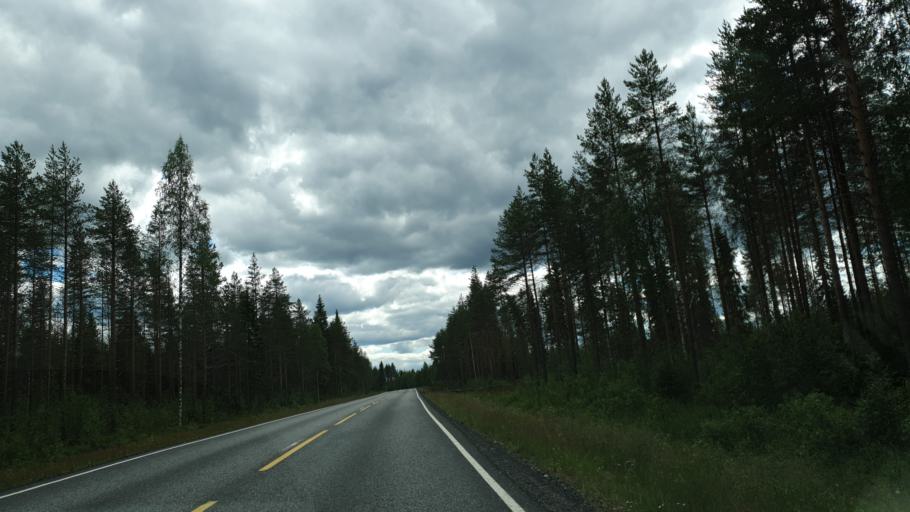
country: FI
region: Kainuu
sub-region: Kehys-Kainuu
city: Kuhmo
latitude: 64.0243
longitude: 29.5966
